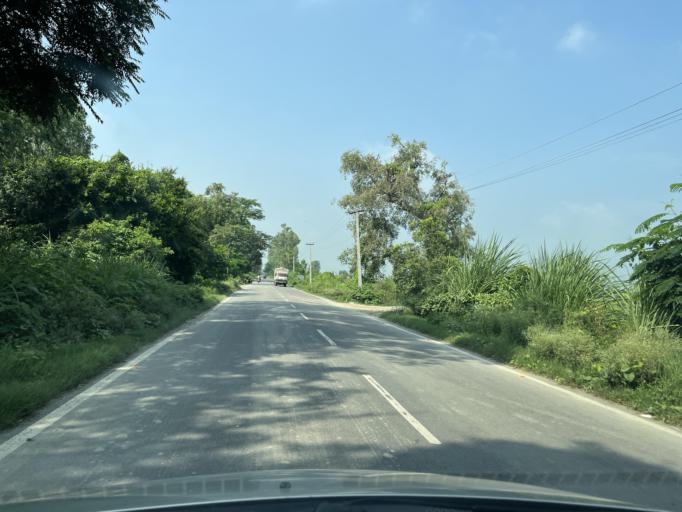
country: IN
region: Uttarakhand
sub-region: Udham Singh Nagar
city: Bazpur
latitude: 29.1874
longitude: 79.1869
